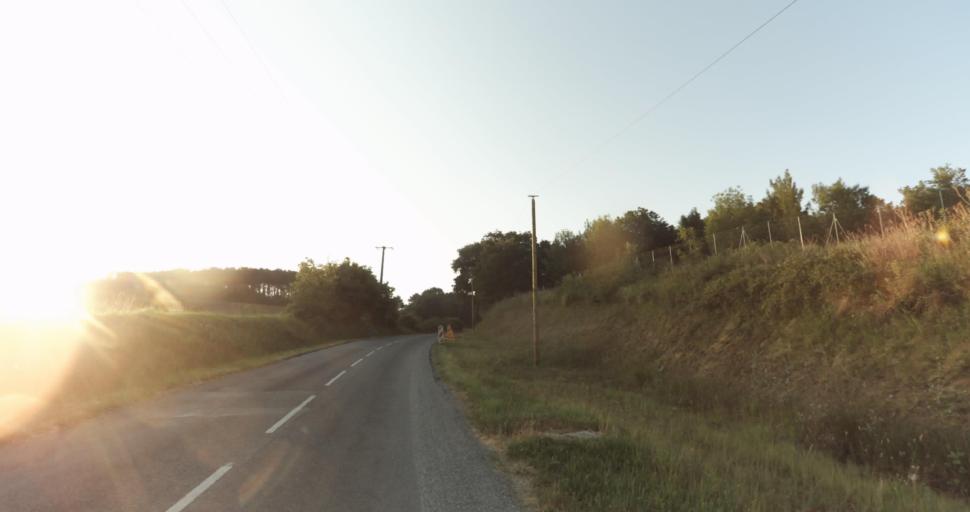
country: FR
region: Midi-Pyrenees
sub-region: Departement du Gers
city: Pujaudran
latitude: 43.6226
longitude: 1.1699
